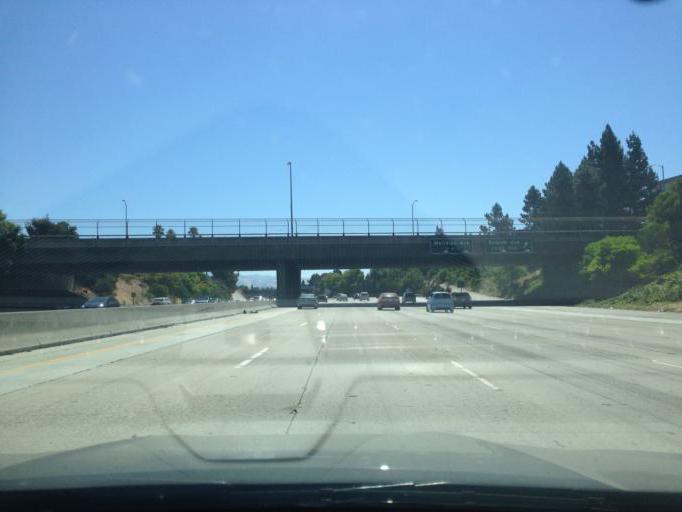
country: US
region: California
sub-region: Santa Clara County
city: Burbank
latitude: 37.3172
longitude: -121.9332
